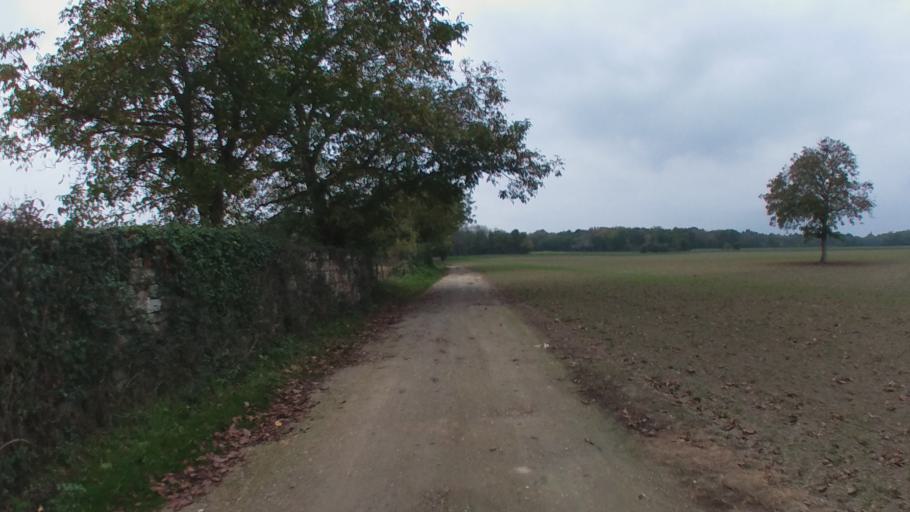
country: FR
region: Pays de la Loire
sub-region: Departement de Maine-et-Loire
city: Distre
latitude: 47.2426
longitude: -0.1275
